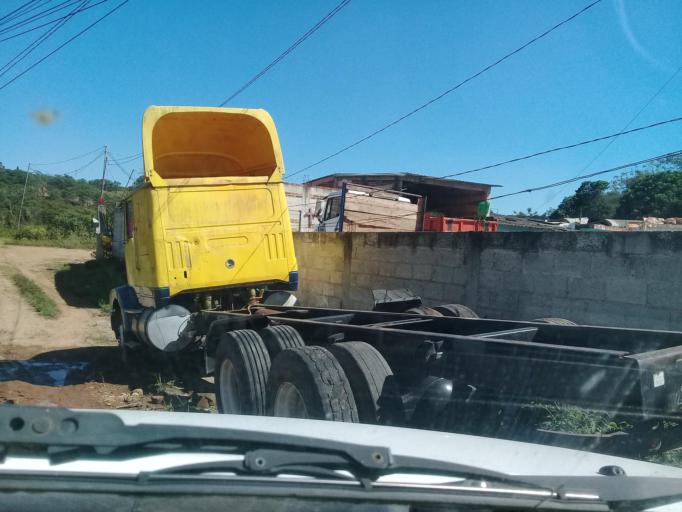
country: MX
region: Veracruz
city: El Castillo
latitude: 19.5513
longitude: -96.8540
